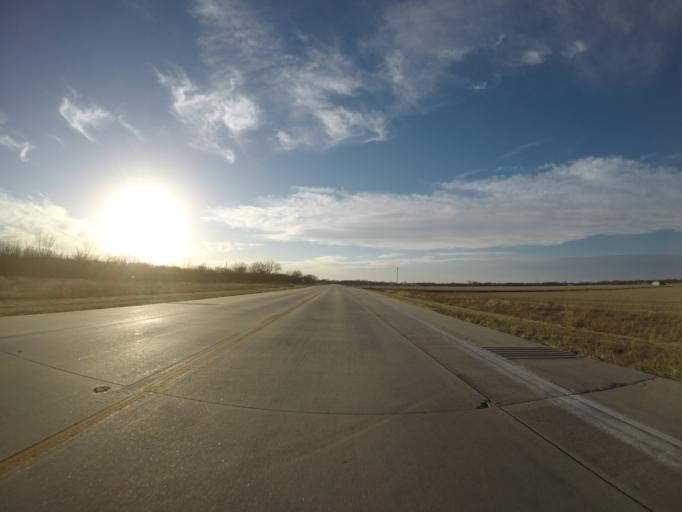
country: US
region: Kansas
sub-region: Chase County
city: Cottonwood Falls
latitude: 38.4069
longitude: -96.3715
